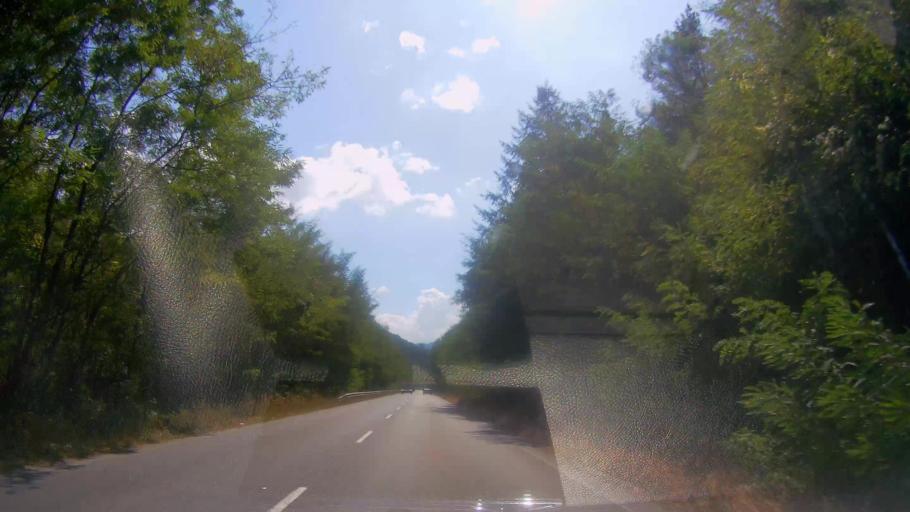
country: BG
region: Stara Zagora
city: Gurkovo
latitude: 42.7555
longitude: 25.7085
